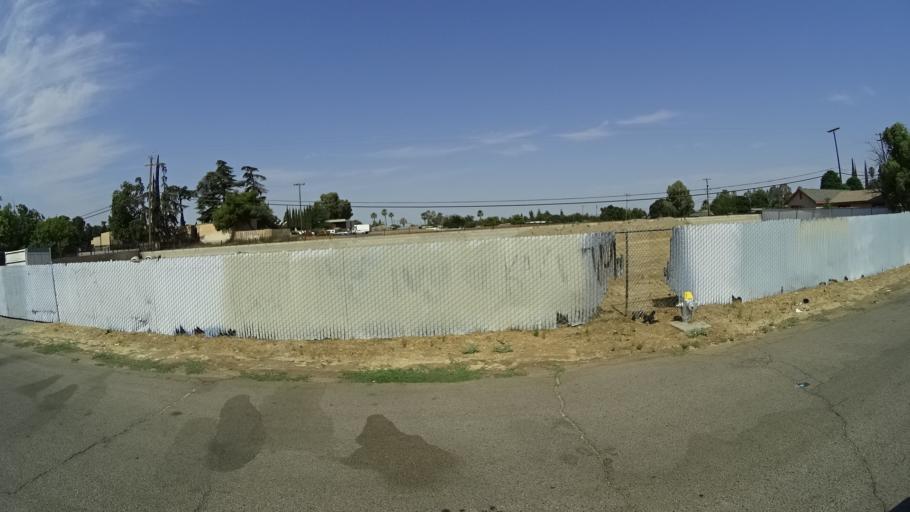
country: US
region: California
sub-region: Fresno County
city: West Park
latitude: 36.7514
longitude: -119.8284
